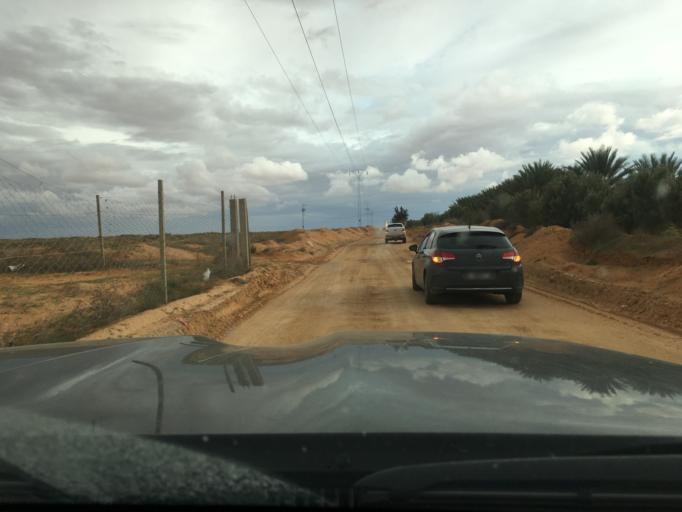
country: TN
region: Madanin
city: Medenine
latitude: 33.2756
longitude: 10.5617
